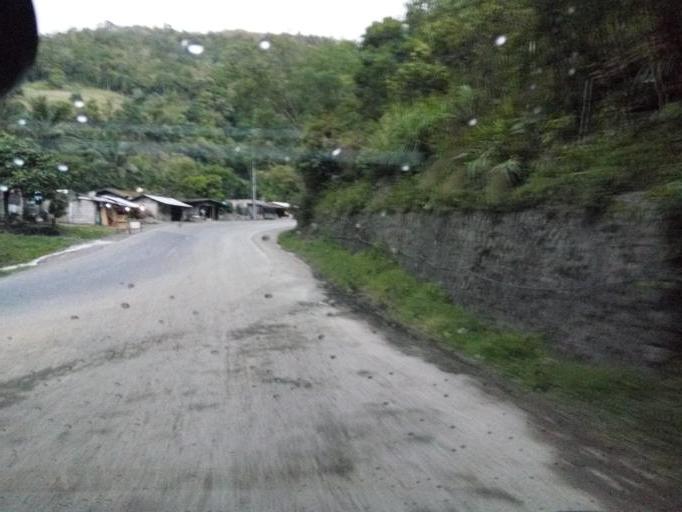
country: PH
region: Cagayan Valley
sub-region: Province of Nueva Vizcaya
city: Santa Fe
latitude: 16.1264
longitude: 120.9348
